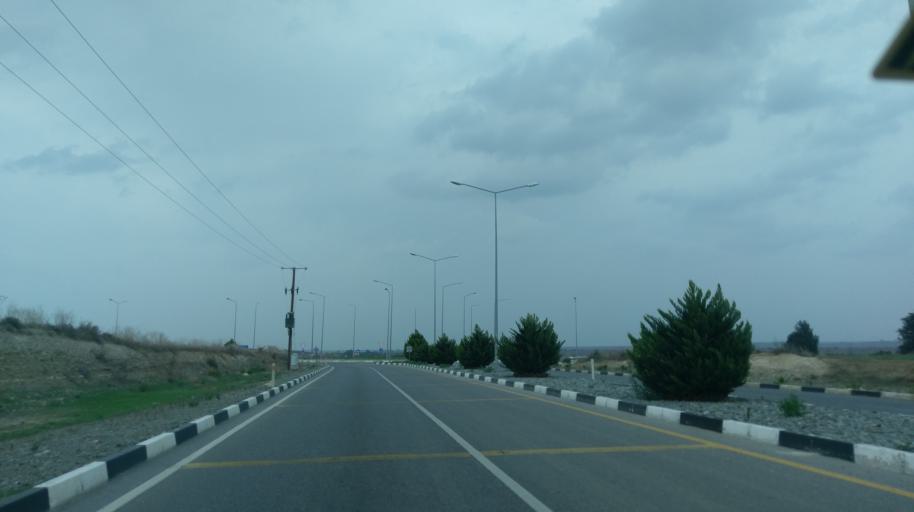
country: CY
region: Lefkosia
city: Morfou
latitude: 35.2044
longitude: 33.0438
